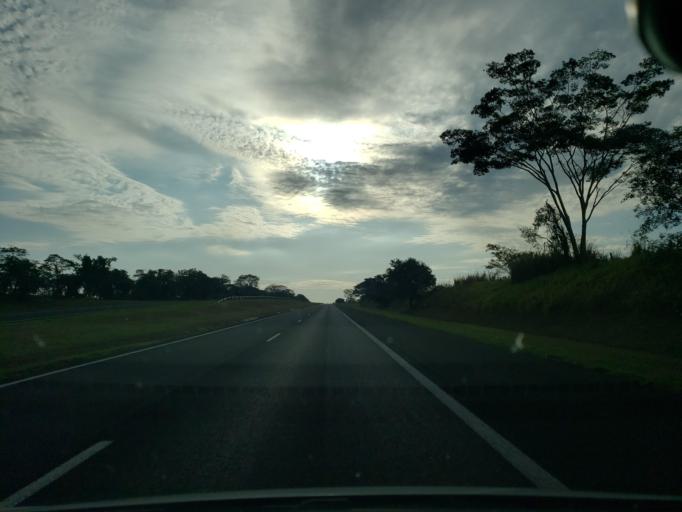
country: BR
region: Sao Paulo
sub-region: Mirandopolis
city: Mirandopolis
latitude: -21.0983
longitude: -51.0435
